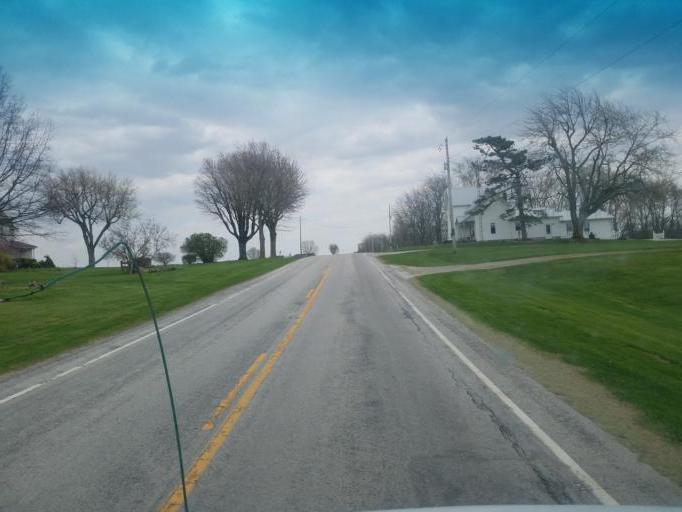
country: US
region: Ohio
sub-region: Seneca County
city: Tiffin
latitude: 40.9499
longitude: -83.1426
